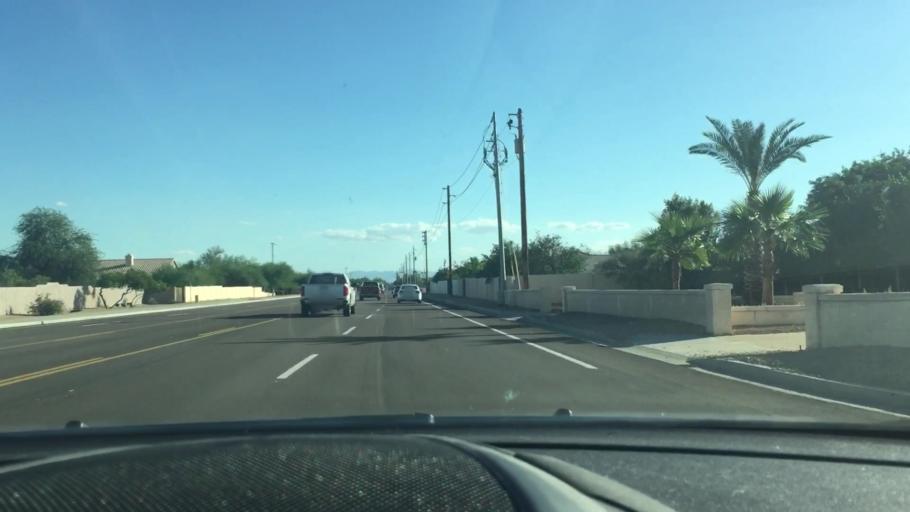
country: US
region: Arizona
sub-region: Maricopa County
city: Sun City
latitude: 33.6943
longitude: -112.2377
